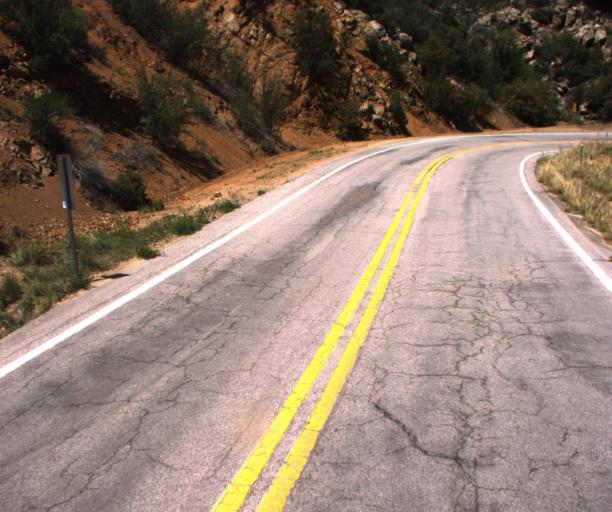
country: US
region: Arizona
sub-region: Yavapai County
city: Prescott
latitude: 34.4515
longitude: -112.5383
